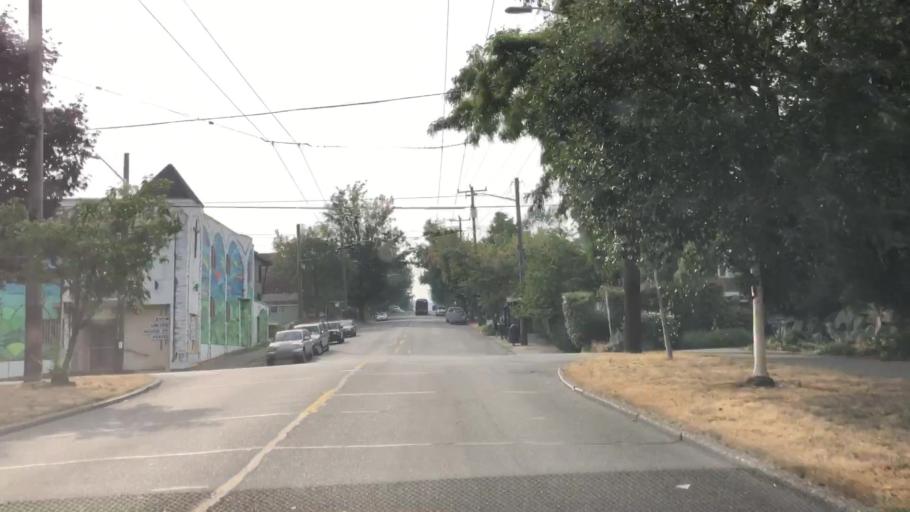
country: US
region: Washington
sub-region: King County
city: Seattle
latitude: 47.6062
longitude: -122.3046
